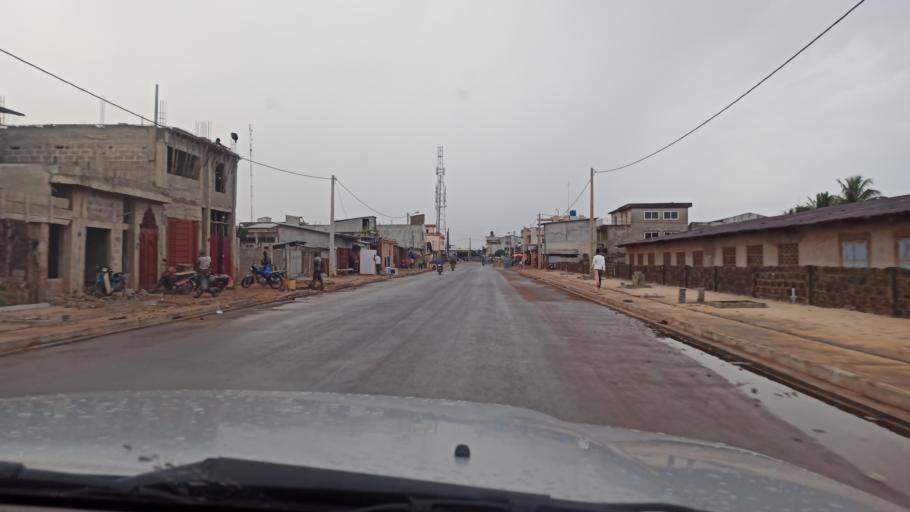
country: BJ
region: Queme
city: Porto-Novo
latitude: 6.4959
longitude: 2.6411
